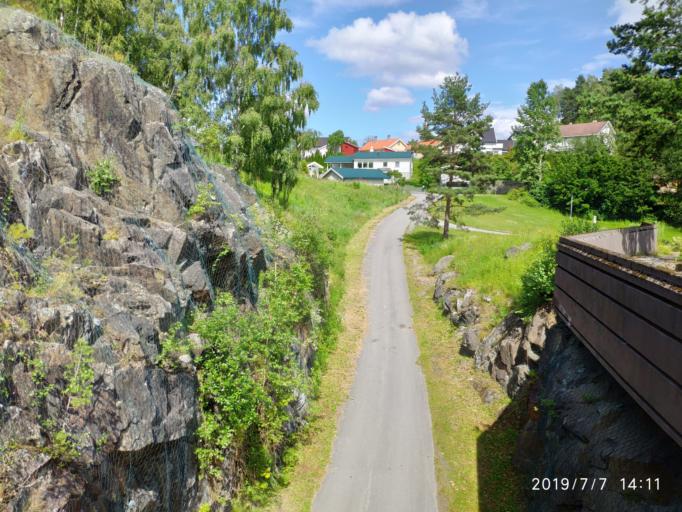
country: NO
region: Buskerud
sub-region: Ringerike
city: Honefoss
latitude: 60.1701
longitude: 10.2545
